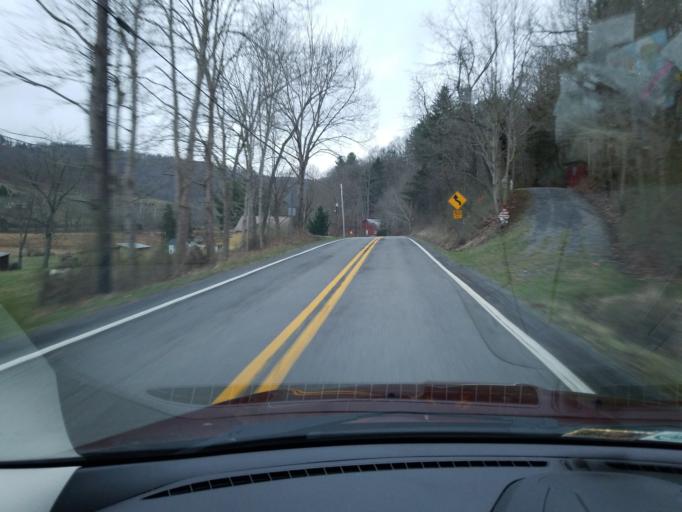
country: US
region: West Virginia
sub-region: Monroe County
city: Union
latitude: 37.5391
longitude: -80.5992
